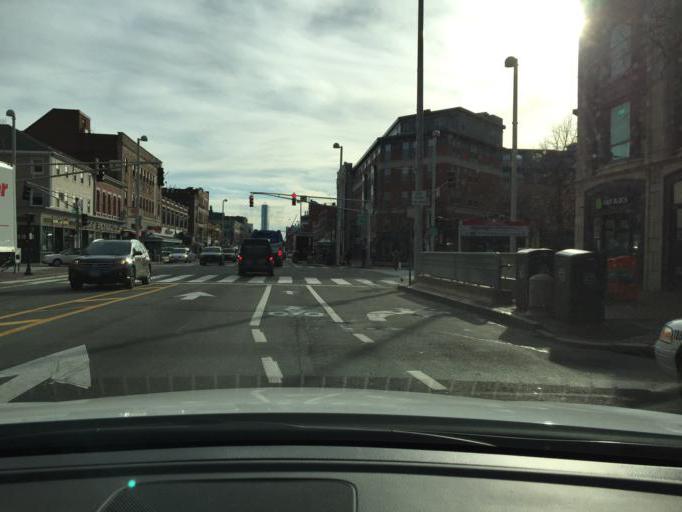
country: US
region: Massachusetts
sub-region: Middlesex County
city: Cambridge
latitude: 42.3659
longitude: -71.1044
